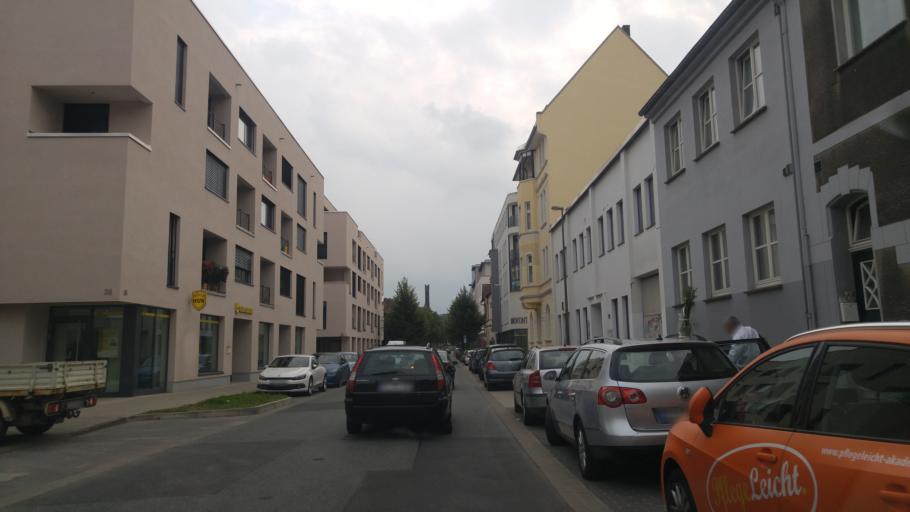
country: DE
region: North Rhine-Westphalia
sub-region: Regierungsbezirk Detmold
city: Bielefeld
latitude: 52.0270
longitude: 8.5432
